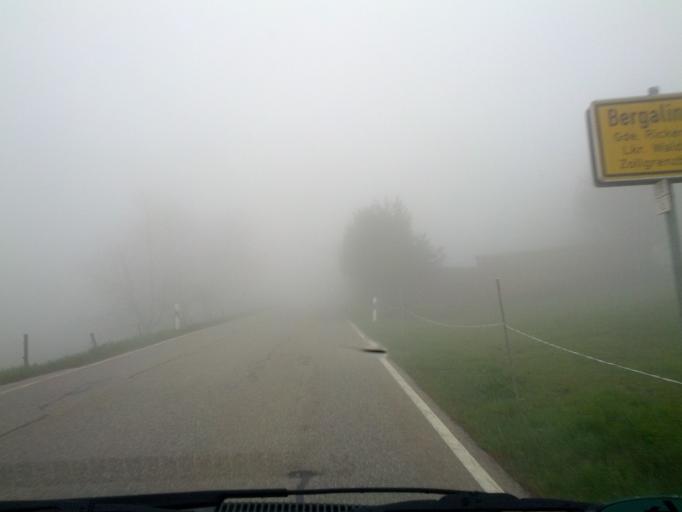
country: DE
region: Baden-Wuerttemberg
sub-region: Freiburg Region
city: Rickenbach
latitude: 47.6135
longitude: 7.9630
